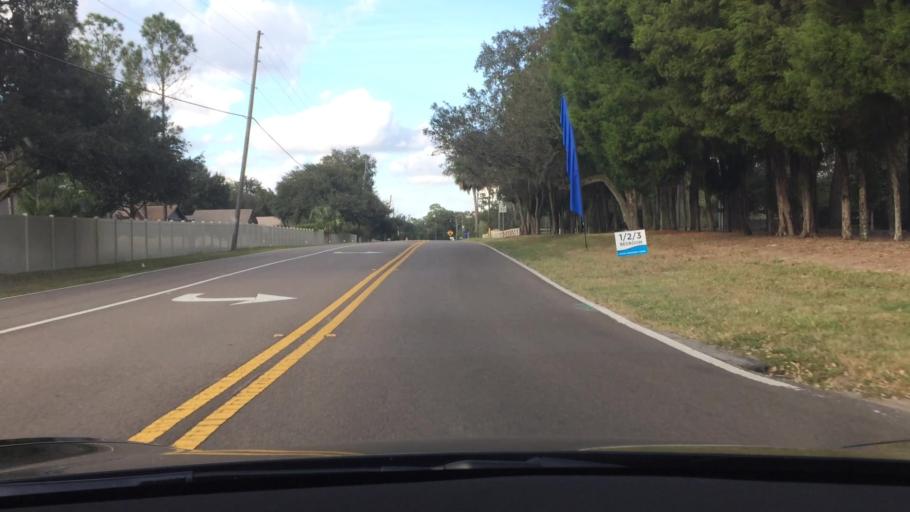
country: US
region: Florida
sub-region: Pasco County
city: Land O' Lakes
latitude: 28.1831
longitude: -82.4032
